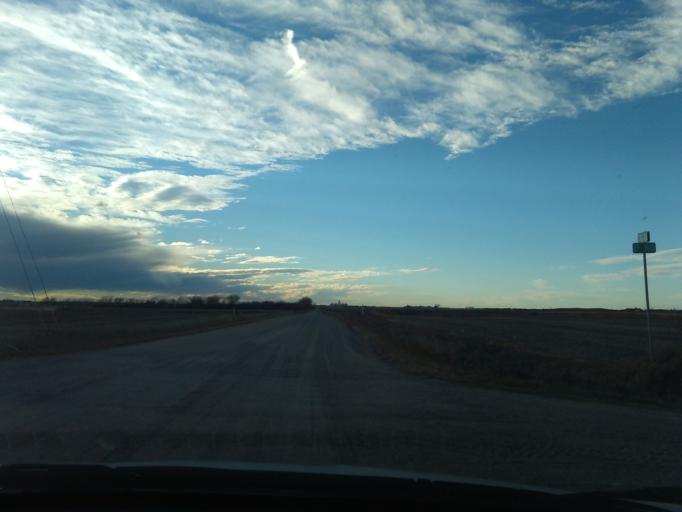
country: US
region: Nebraska
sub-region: Phelps County
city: Holdrege
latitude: 40.4085
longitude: -99.3419
